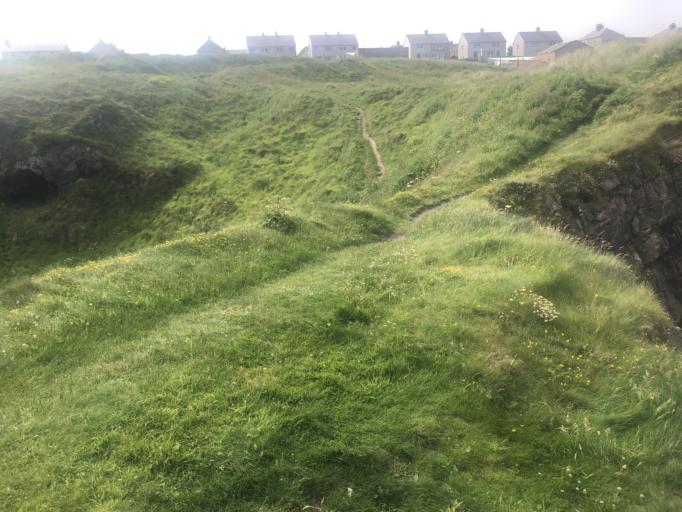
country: GB
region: Scotland
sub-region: Moray
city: Portknockie
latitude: 57.7059
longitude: -2.8537
